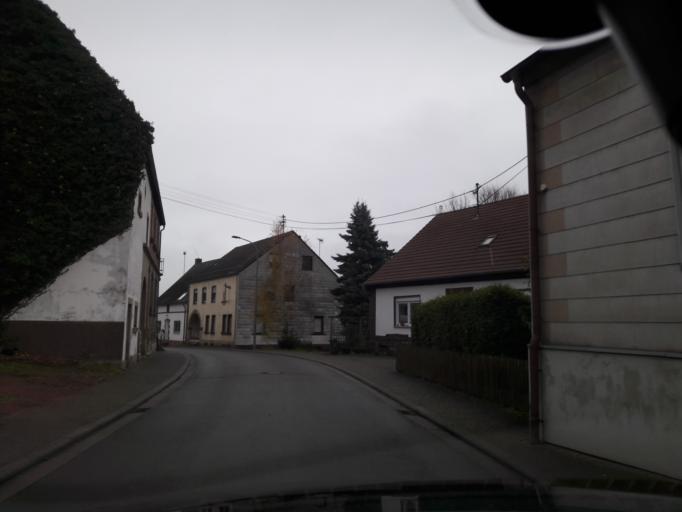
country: DE
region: Rheinland-Pfalz
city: Wahnwegen
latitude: 49.4659
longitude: 7.4057
